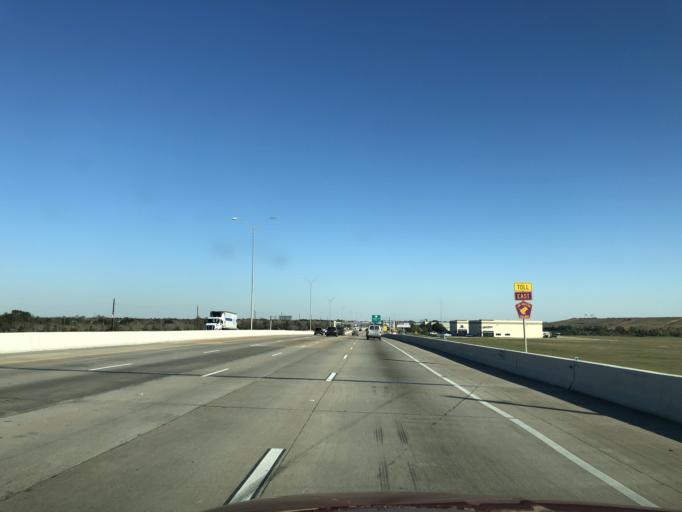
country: US
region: Texas
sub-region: Fort Bend County
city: Fresno
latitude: 29.5963
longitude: -95.4456
